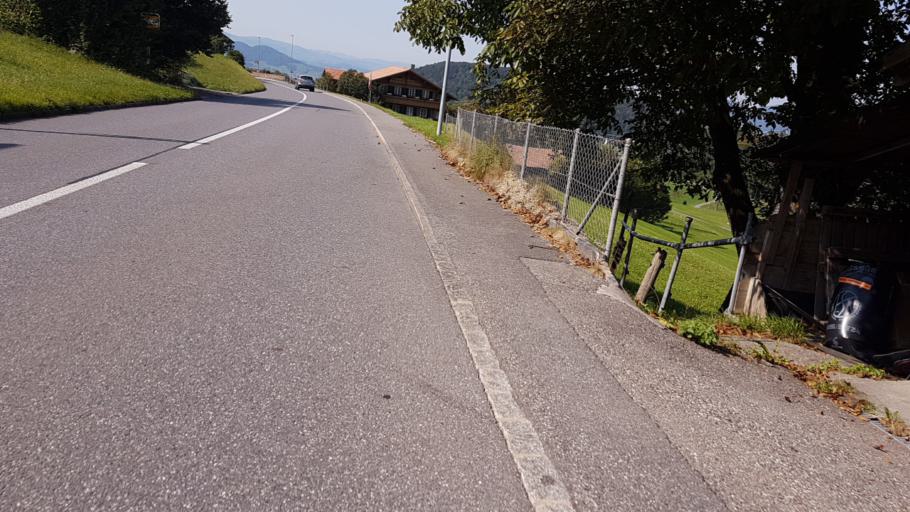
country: CH
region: Bern
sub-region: Frutigen-Niedersimmental District
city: Aeschi
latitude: 46.6622
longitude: 7.6920
